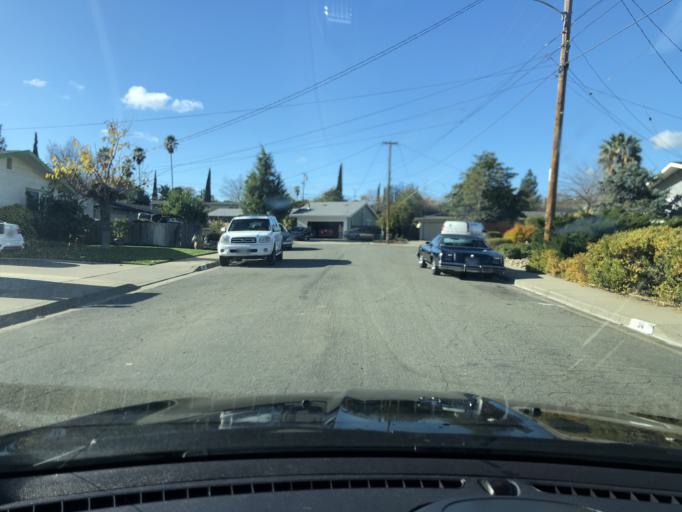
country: US
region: California
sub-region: Contra Costa County
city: Pacheco
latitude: 37.9847
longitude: -122.0730
